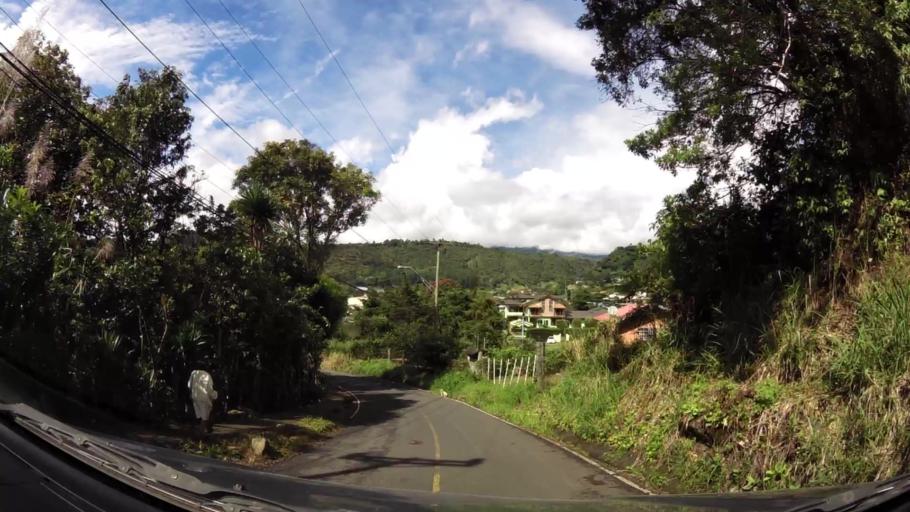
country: PA
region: Chiriqui
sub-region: Distrito Boquete
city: Boquete
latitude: 8.7750
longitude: -82.4289
